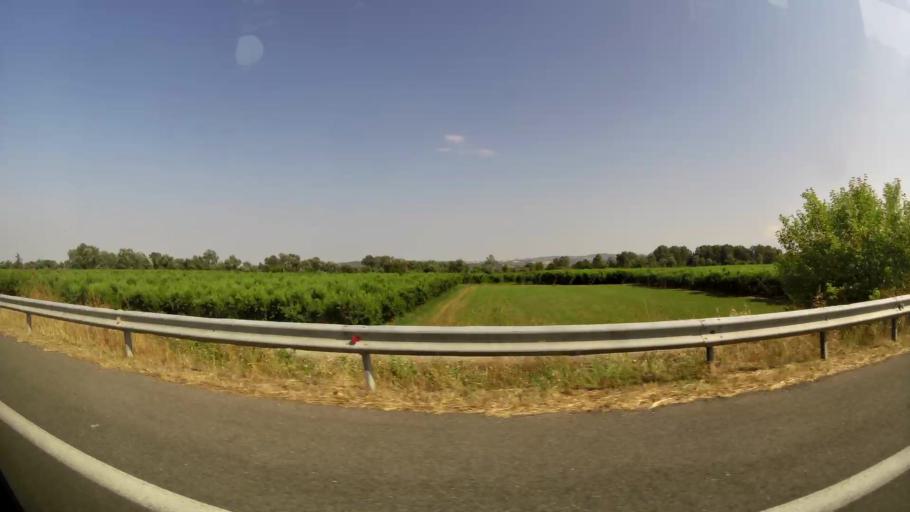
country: GR
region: Central Macedonia
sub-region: Nomos Imathias
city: Loutros
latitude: 40.5834
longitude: 22.4131
